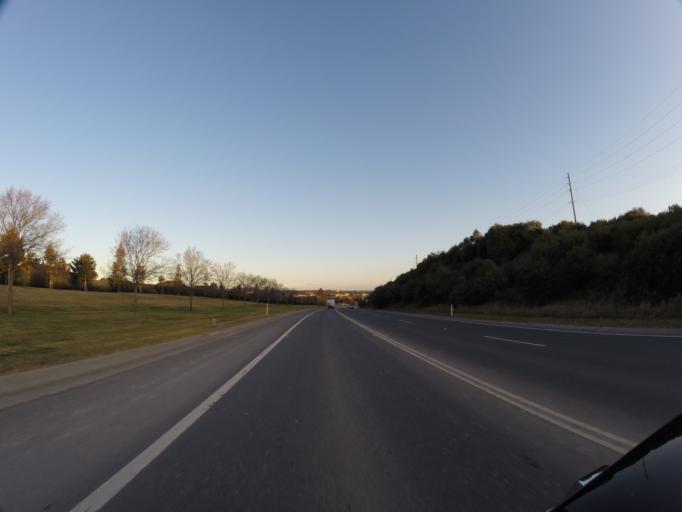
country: AU
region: New South Wales
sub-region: Camden
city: Narellan
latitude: -34.0224
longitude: 150.7262
